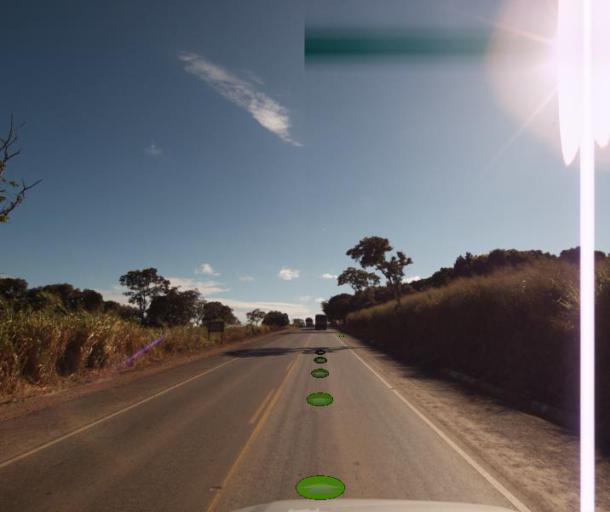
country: BR
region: Goias
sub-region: Uruacu
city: Uruacu
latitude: -14.6384
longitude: -49.1786
